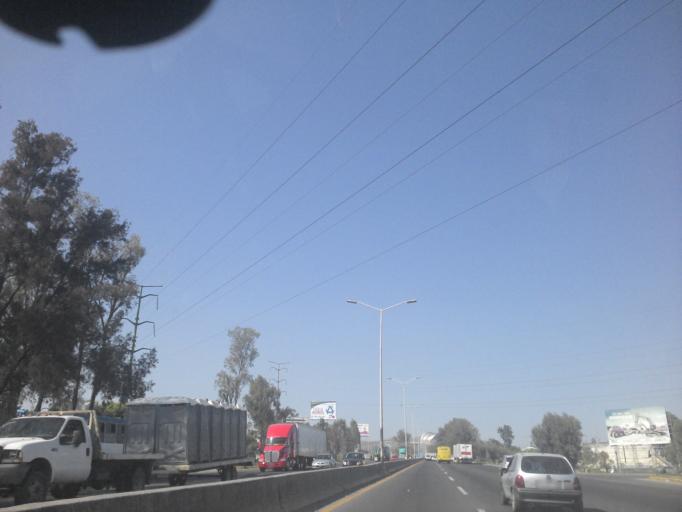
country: MX
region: Jalisco
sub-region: San Pedro Tlaquepaque
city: Paseo del Prado
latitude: 20.5919
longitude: -103.3869
